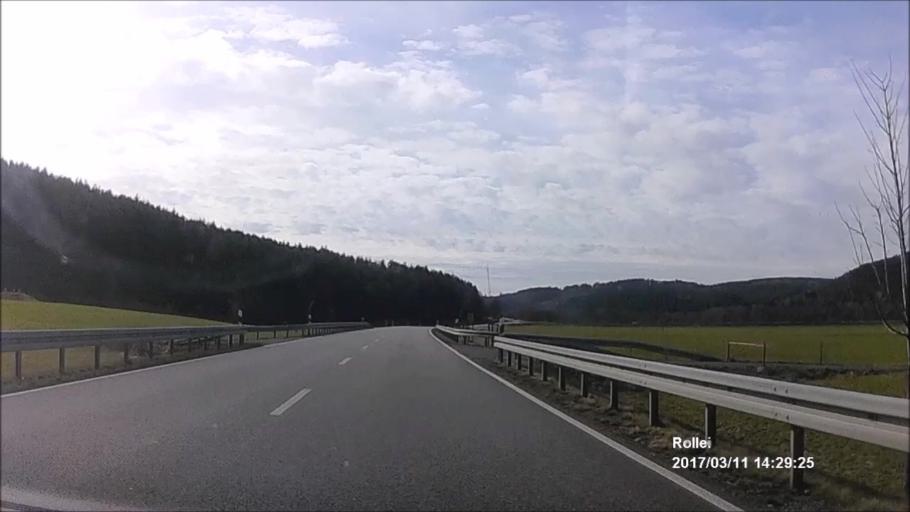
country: DE
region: Thuringia
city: Schleusingen
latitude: 50.4928
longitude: 10.7279
